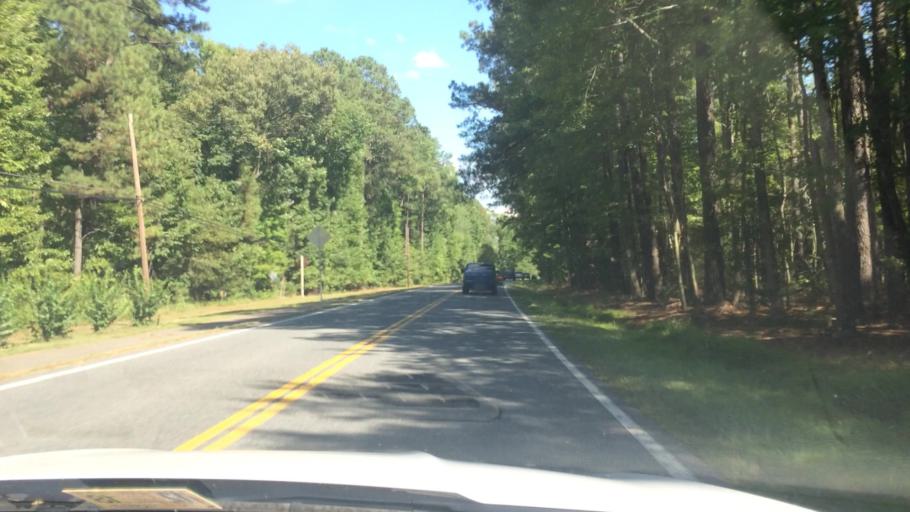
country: US
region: Virginia
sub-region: Charles City County
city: Charles City
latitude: 37.2915
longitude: -76.9329
